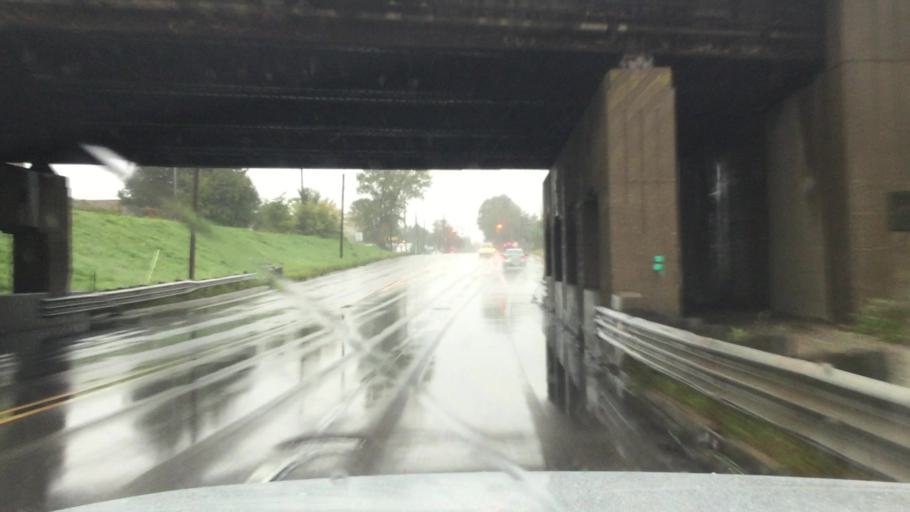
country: US
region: Michigan
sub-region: Saginaw County
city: Buena Vista
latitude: 43.4148
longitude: -83.9067
